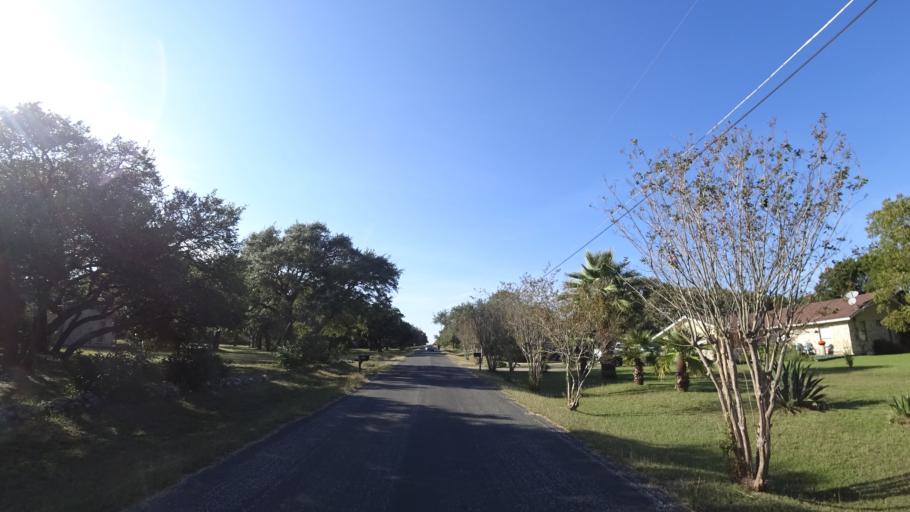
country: US
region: Texas
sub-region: Travis County
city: Barton Creek
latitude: 30.2455
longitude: -97.9087
